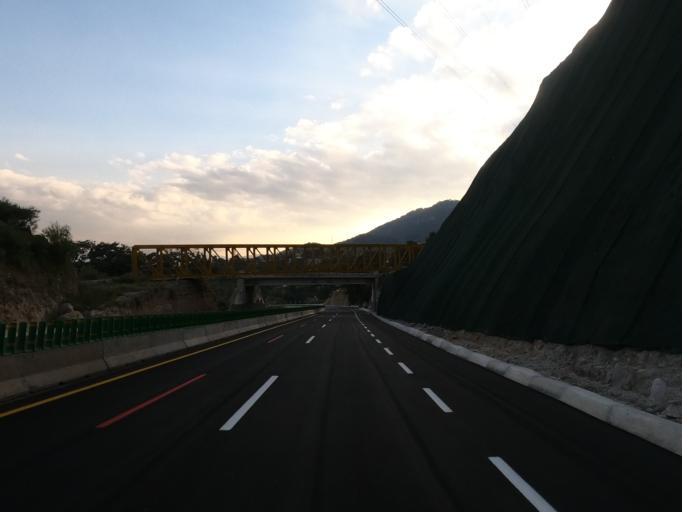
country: MX
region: Mexico
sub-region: Naucalpan de Juarez
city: Llano de las Flores (Barrio del Hueso)
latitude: 19.4297
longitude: -99.3316
